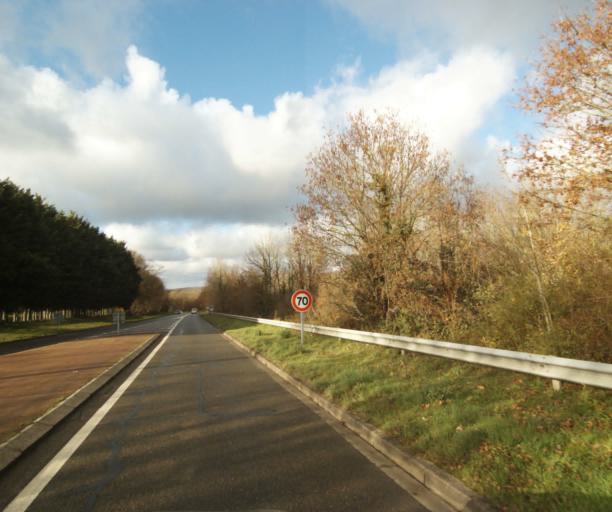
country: FR
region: Ile-de-France
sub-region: Departement des Yvelines
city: Meulan-en-Yvelines
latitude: 49.0140
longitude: 1.9243
